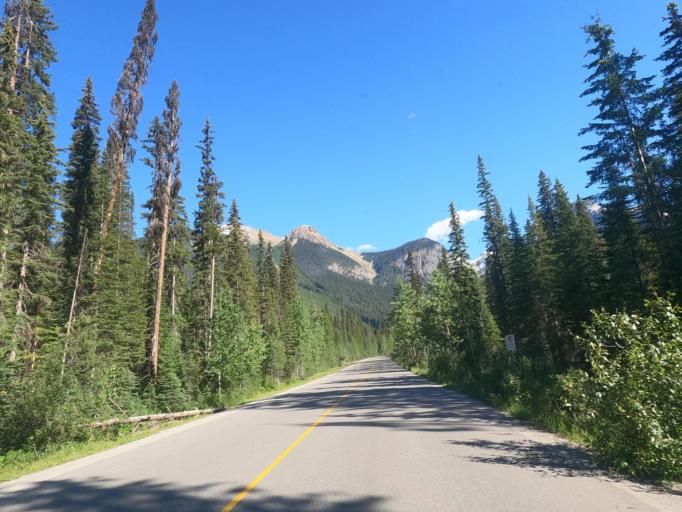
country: CA
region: Alberta
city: Lake Louise
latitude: 51.4335
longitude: -116.5383
